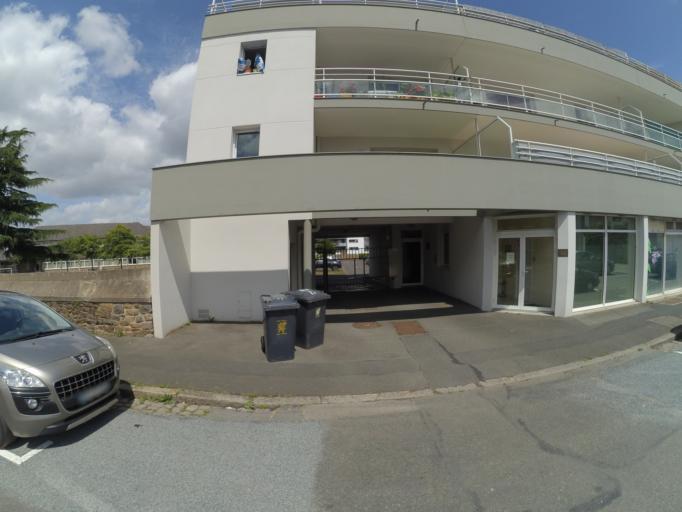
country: FR
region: Brittany
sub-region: Departement des Cotes-d'Armor
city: Saint-Brieuc
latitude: 48.5049
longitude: -2.7680
